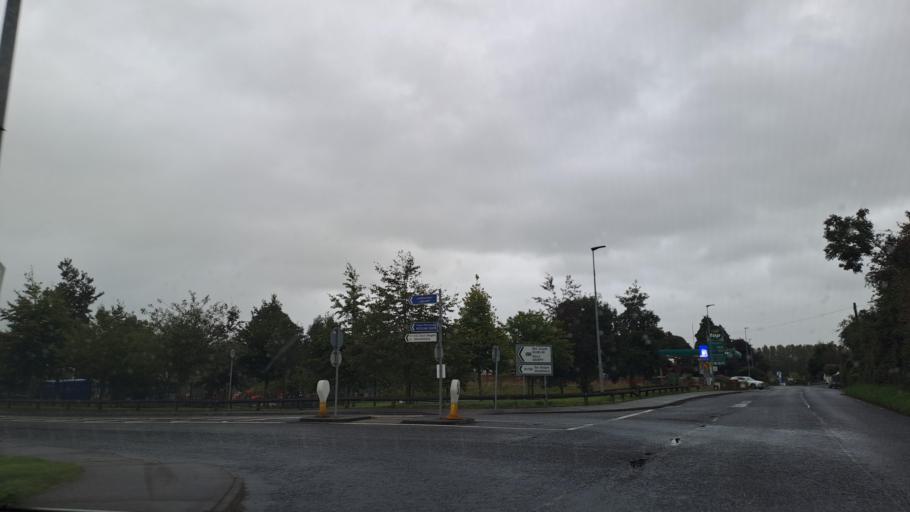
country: IE
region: Ulster
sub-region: County Monaghan
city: Carrickmacross
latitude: 53.9675
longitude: -6.7151
